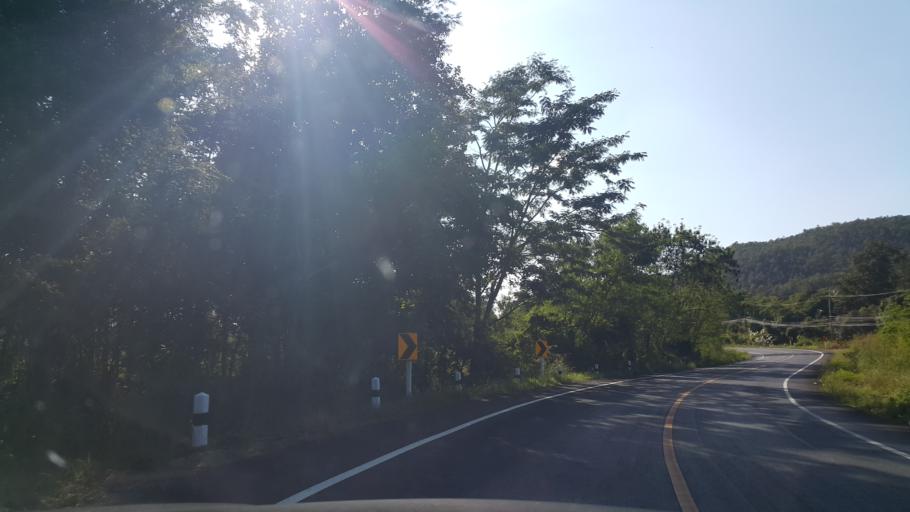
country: TH
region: Lamphun
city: Mae Tha
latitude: 18.4684
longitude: 99.1534
